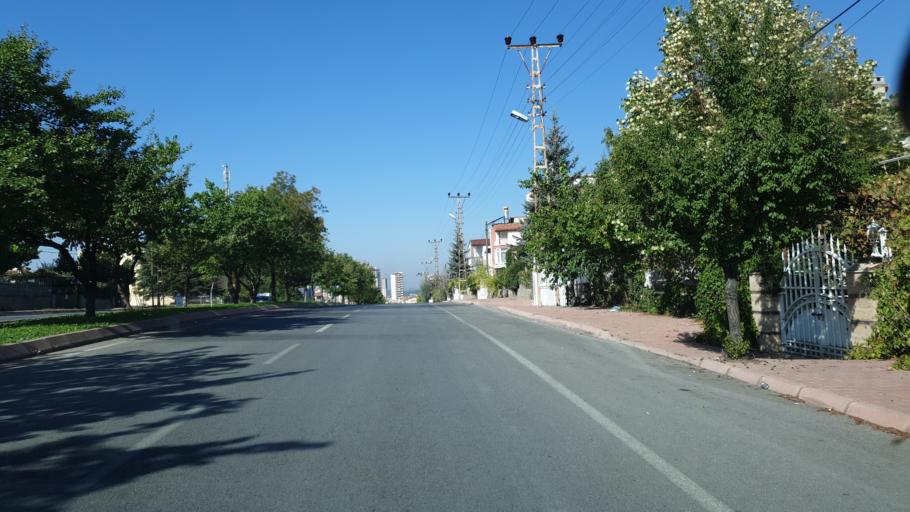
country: TR
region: Kayseri
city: Kocasinan
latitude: 38.7776
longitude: 35.5876
